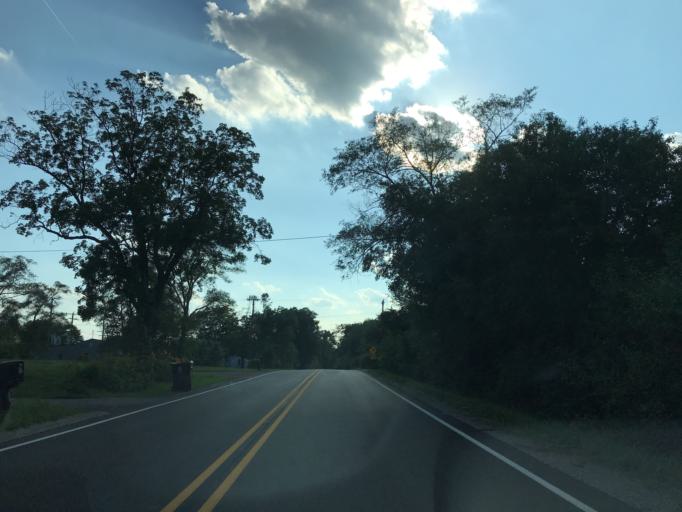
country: US
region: Michigan
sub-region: Washtenaw County
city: Ypsilanti
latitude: 42.3247
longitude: -83.6092
